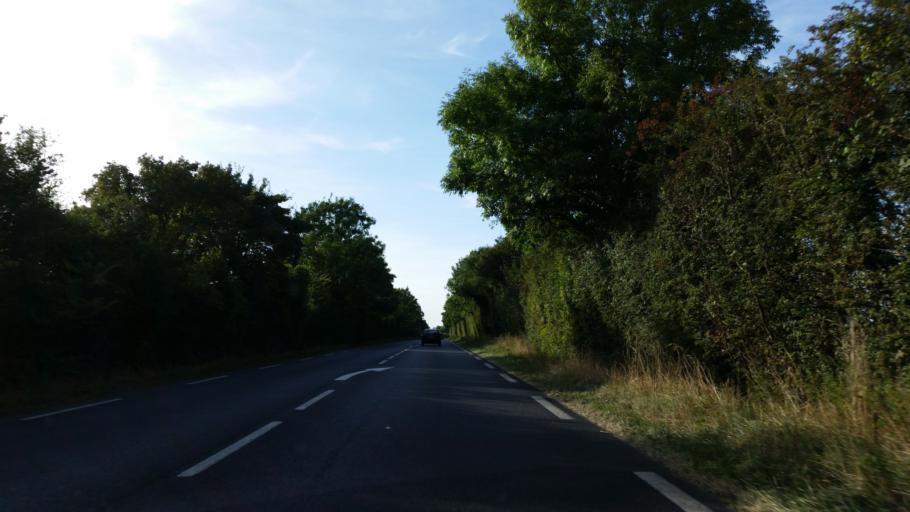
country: FR
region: Lower Normandy
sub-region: Departement du Calvados
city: Cambremer
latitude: 49.1356
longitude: -0.0039
